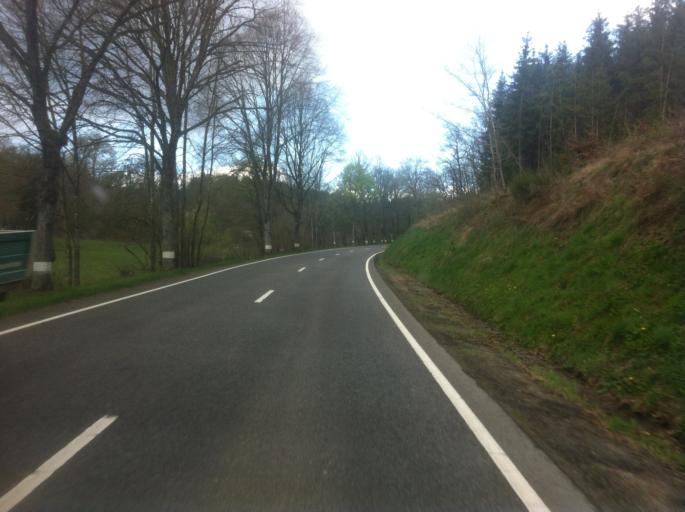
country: LU
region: Diekirch
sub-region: Canton de Wiltz
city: Eschweiler
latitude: 49.9782
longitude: 5.9581
